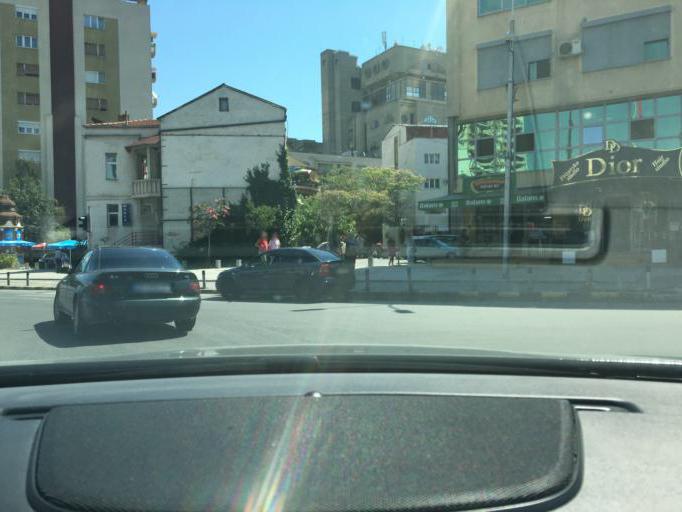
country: MK
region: Karpos
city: Skopje
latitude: 41.9974
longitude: 21.4281
